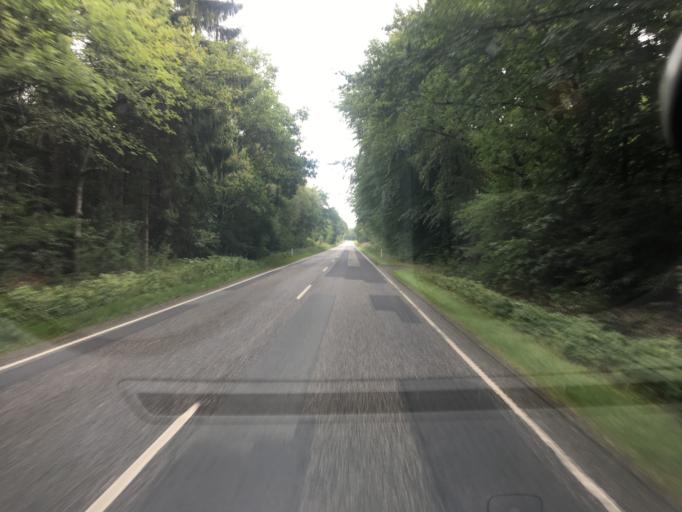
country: DK
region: South Denmark
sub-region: Tonder Kommune
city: Toftlund
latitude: 55.1232
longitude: 9.1003
